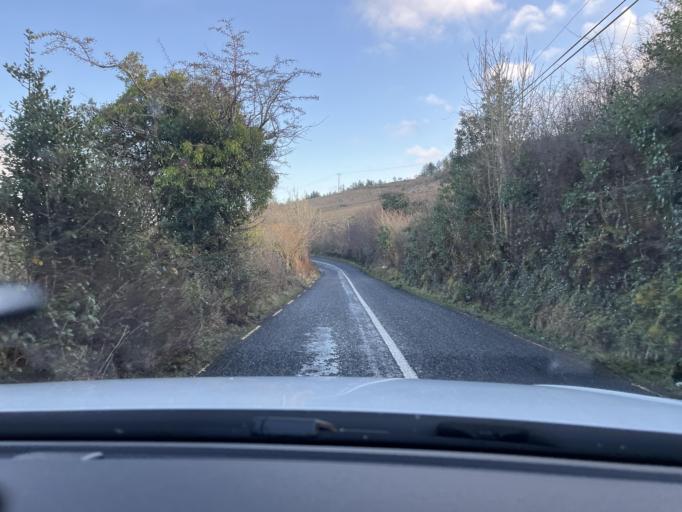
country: IE
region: Connaught
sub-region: County Leitrim
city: Manorhamilton
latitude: 54.1999
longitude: -7.9470
